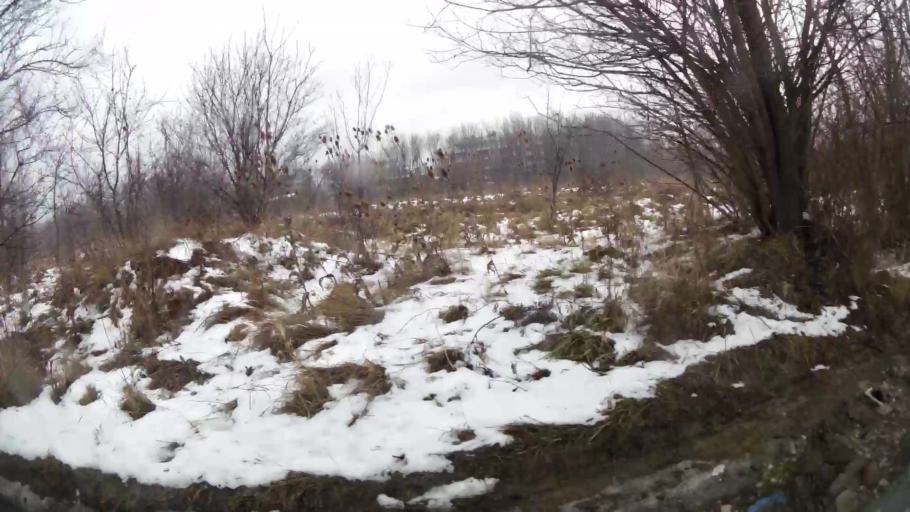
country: BG
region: Sofia-Capital
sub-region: Stolichna Obshtina
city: Sofia
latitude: 42.6545
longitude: 23.2995
